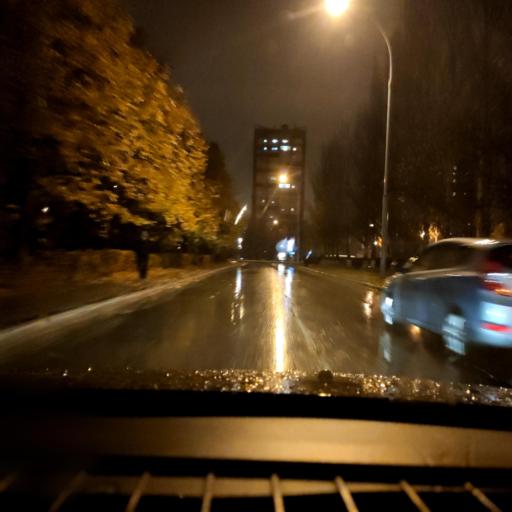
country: RU
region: Samara
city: Tol'yatti
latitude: 53.5283
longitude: 49.3038
